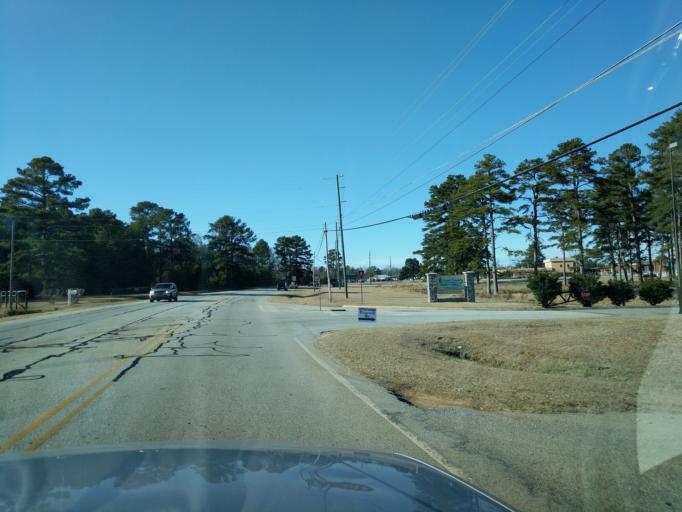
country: US
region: Georgia
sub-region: Hart County
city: Hartwell
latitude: 34.3353
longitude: -82.9186
